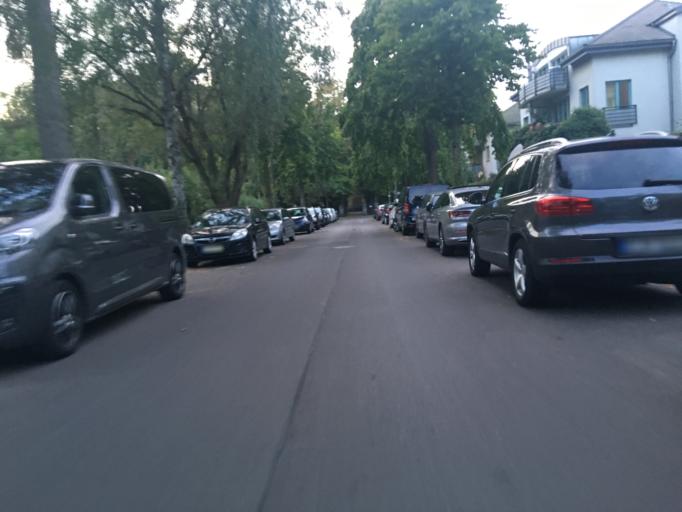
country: DE
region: Berlin
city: Fennpfuhl
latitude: 52.5455
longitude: 13.4818
